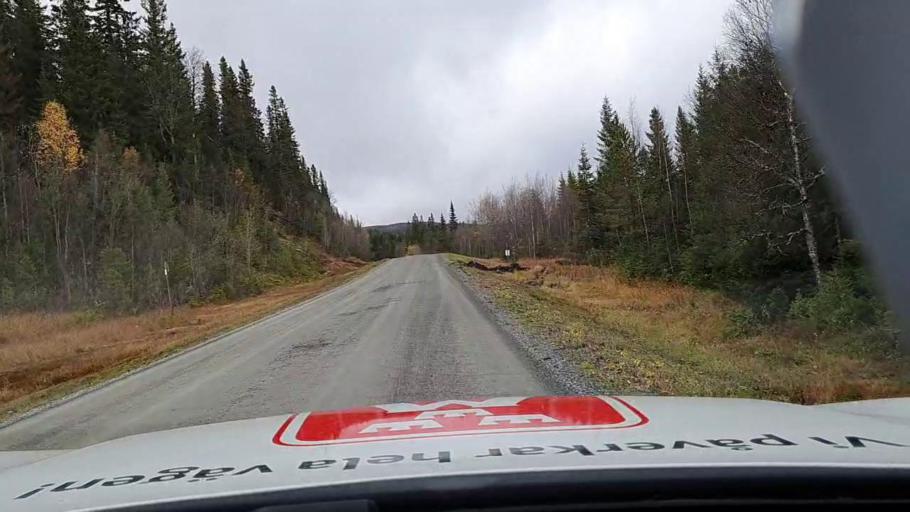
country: SE
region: Jaemtland
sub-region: Bergs Kommun
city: Hoverberg
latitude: 63.0404
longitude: 13.9642
